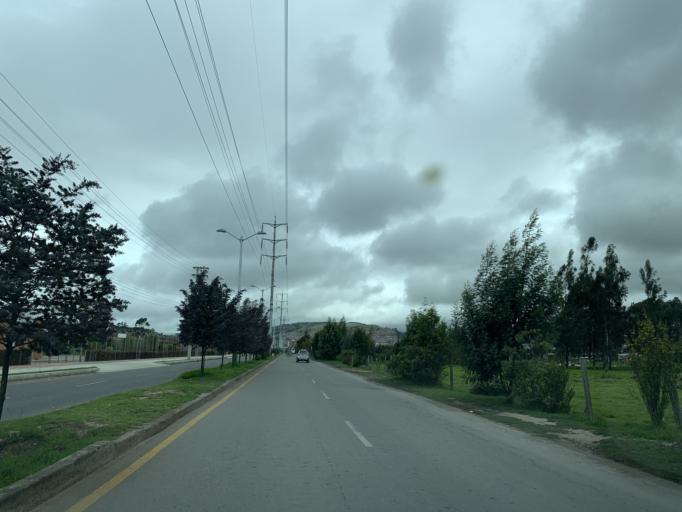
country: CO
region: Boyaca
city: Tunja
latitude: 5.5683
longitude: -73.3327
